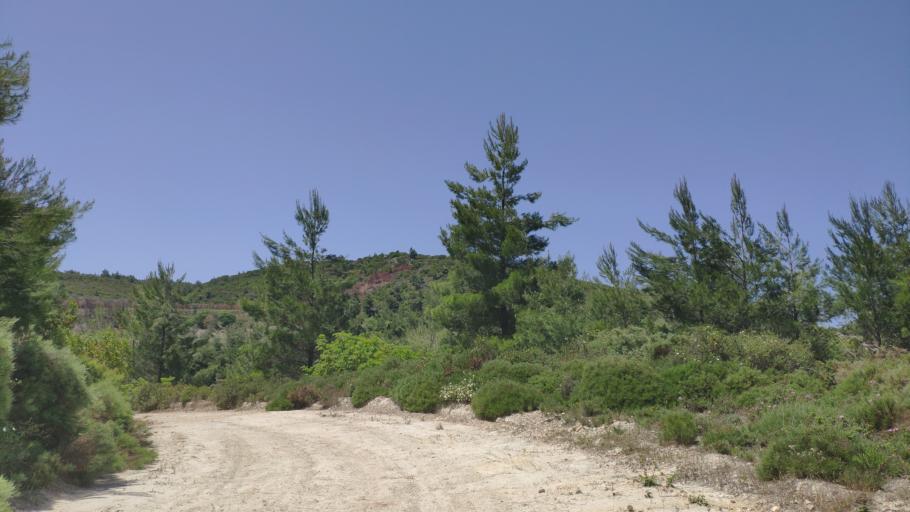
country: GR
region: Attica
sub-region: Nomarchia Anatolikis Attikis
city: Kalamos
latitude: 38.2775
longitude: 23.8486
